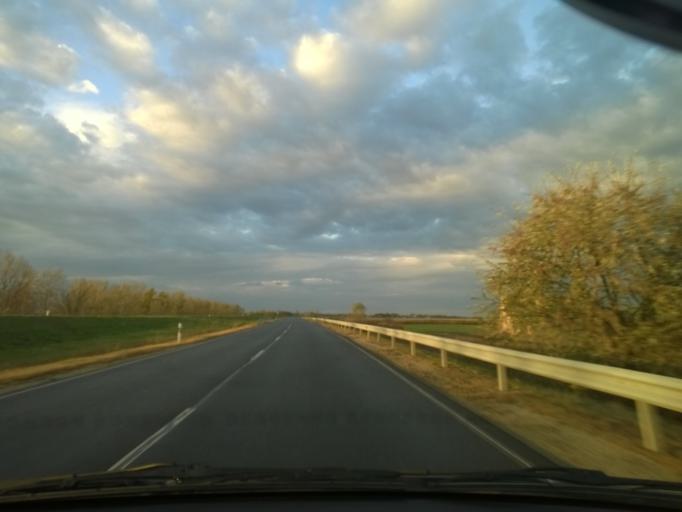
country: HU
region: Bacs-Kiskun
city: Solt
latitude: 46.7624
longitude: 19.0102
